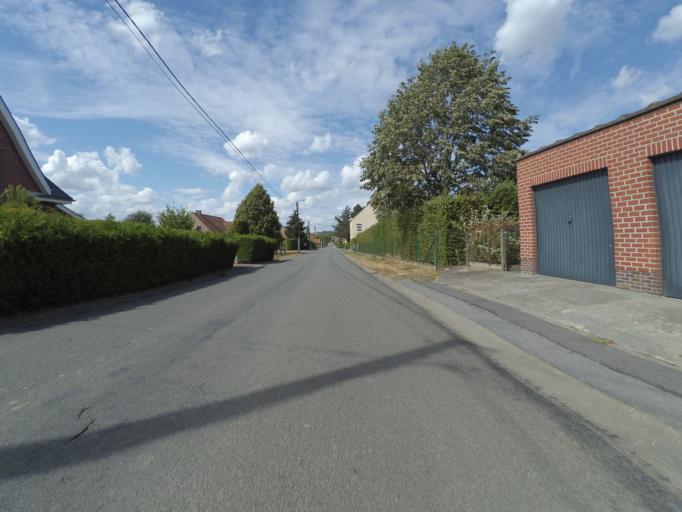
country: BE
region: Flanders
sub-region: Provincie Oost-Vlaanderen
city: Ronse
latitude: 50.7290
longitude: 3.5992
